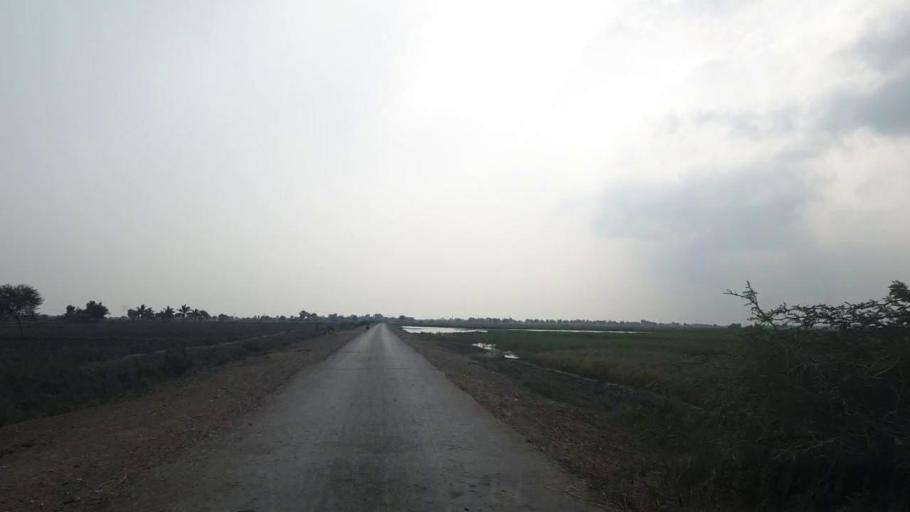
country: PK
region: Sindh
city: Badin
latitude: 24.6492
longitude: 68.6991
